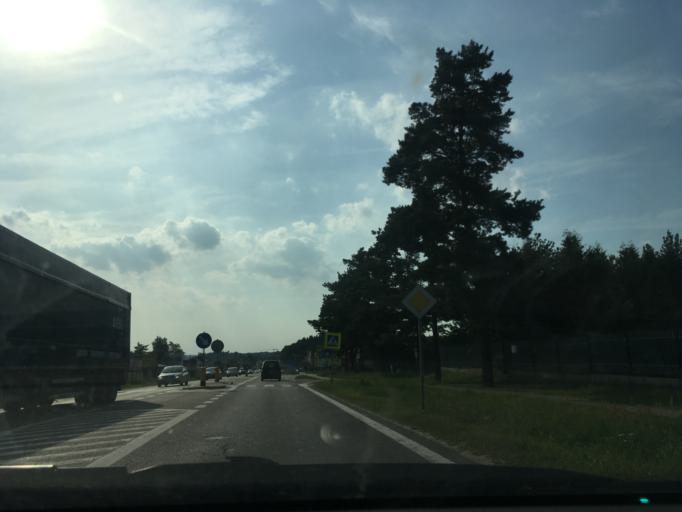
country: PL
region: Podlasie
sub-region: Bialystok
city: Bialystok
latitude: 53.1254
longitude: 23.2466
